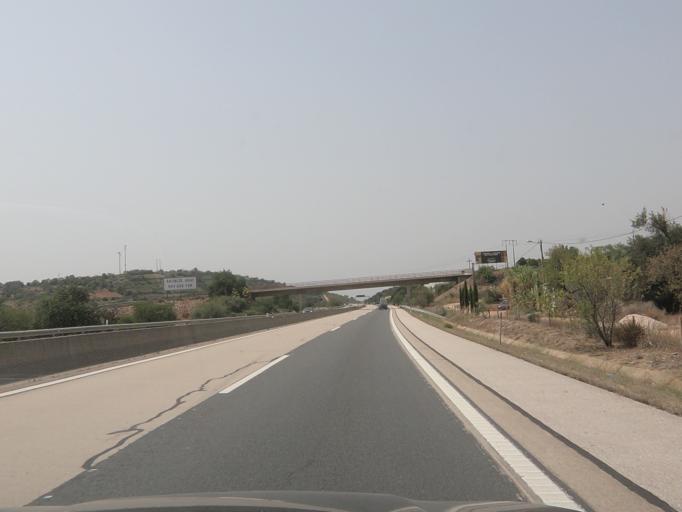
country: PT
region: Faro
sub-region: Loule
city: Boliqueime
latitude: 37.1501
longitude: -8.1686
